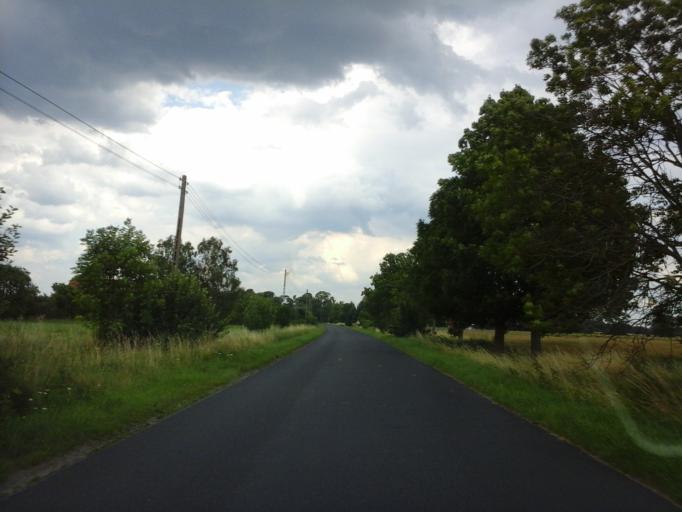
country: PL
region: West Pomeranian Voivodeship
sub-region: Powiat choszczenski
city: Bierzwnik
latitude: 53.0468
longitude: 15.7327
